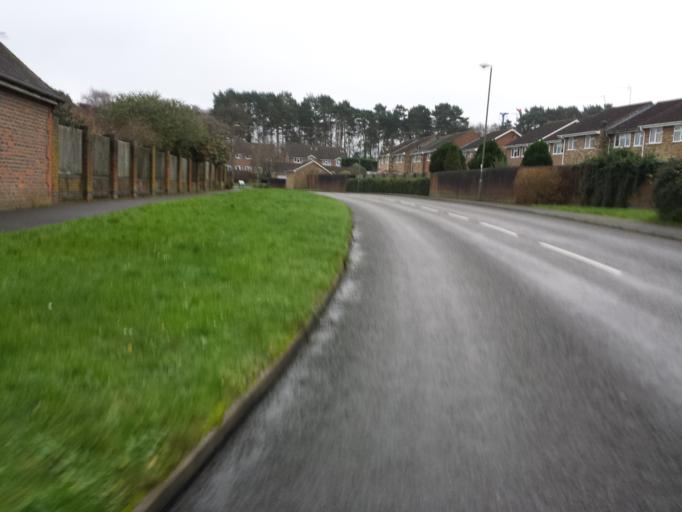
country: GB
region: England
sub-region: Surrey
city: Bagshot
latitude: 51.3544
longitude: -0.6910
